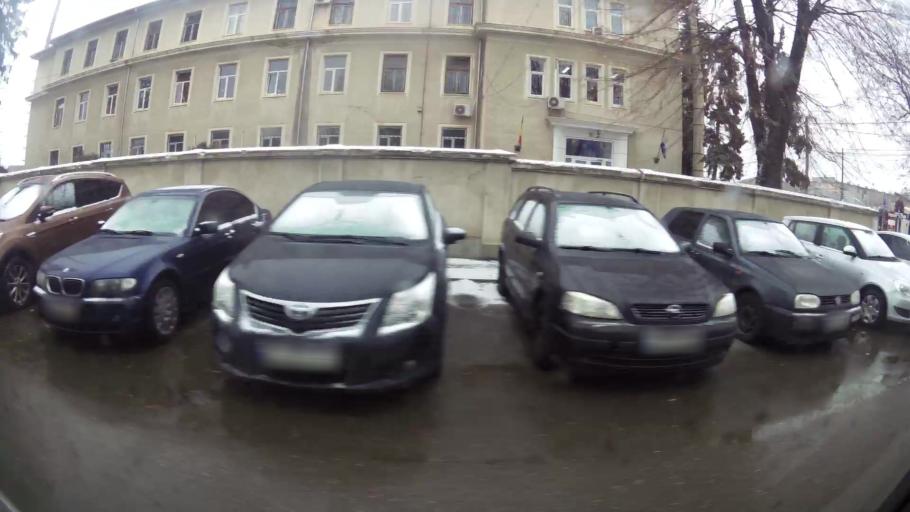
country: RO
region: Prahova
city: Ploiesti
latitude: 44.9395
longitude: 26.0117
